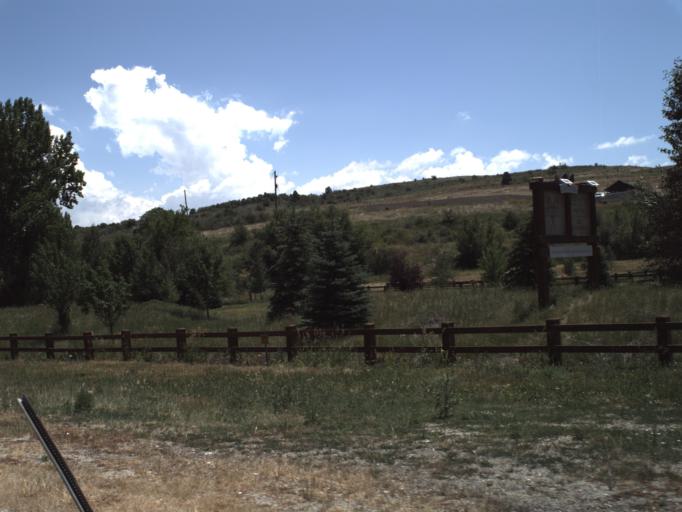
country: US
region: Utah
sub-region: Weber County
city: Wolf Creek
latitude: 41.2464
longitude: -111.7718
